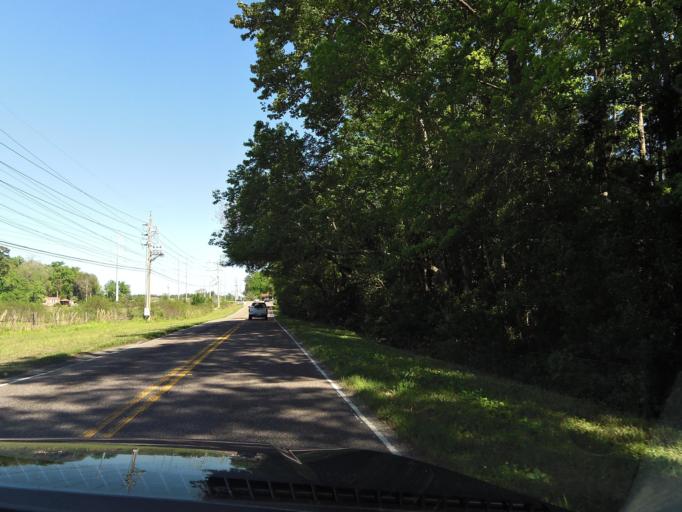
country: US
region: Florida
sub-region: Duval County
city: Jacksonville
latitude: 30.4548
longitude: -81.5992
